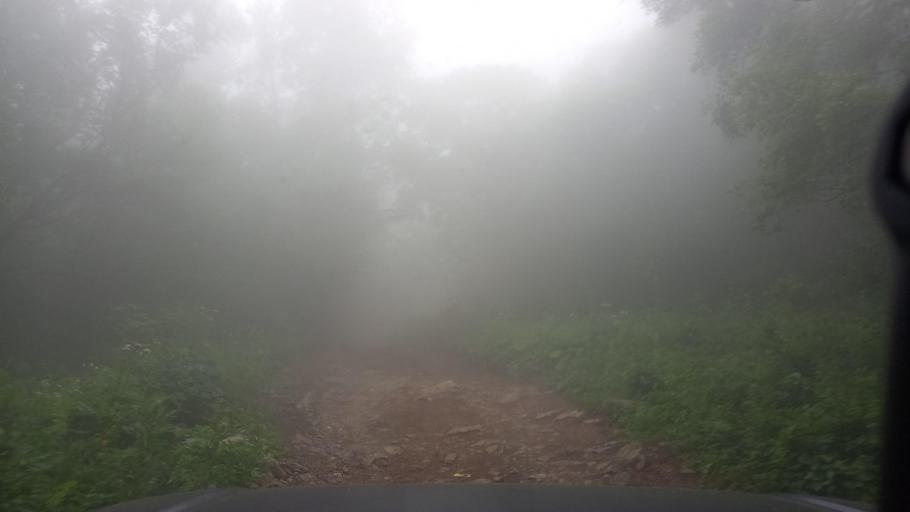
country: RU
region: Karachayevo-Cherkesiya
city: Kurdzhinovo
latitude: 43.7994
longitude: 40.8430
